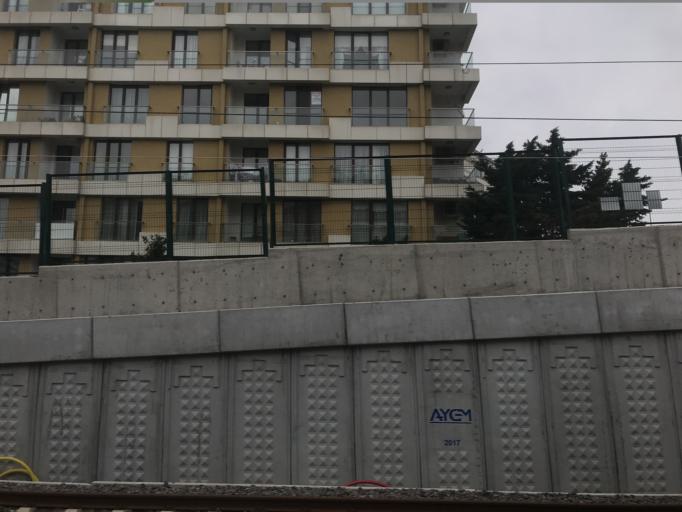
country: TR
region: Istanbul
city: Maltepe
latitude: 40.9161
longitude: 29.1441
